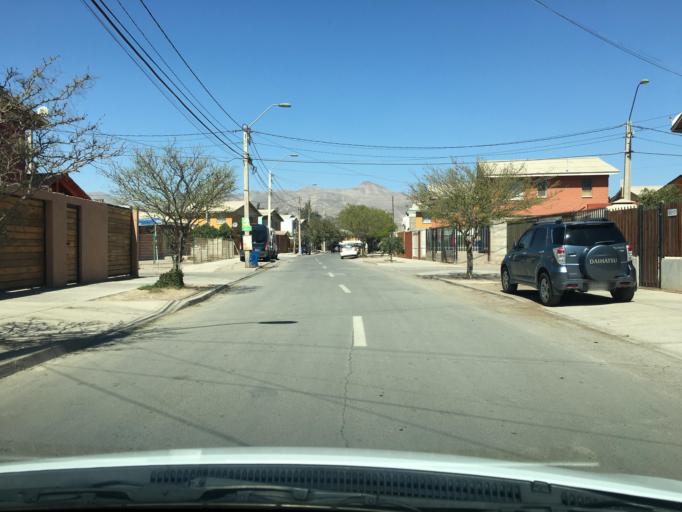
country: CL
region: Atacama
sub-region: Provincia de Copiapo
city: Copiapo
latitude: -27.4100
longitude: -70.2835
